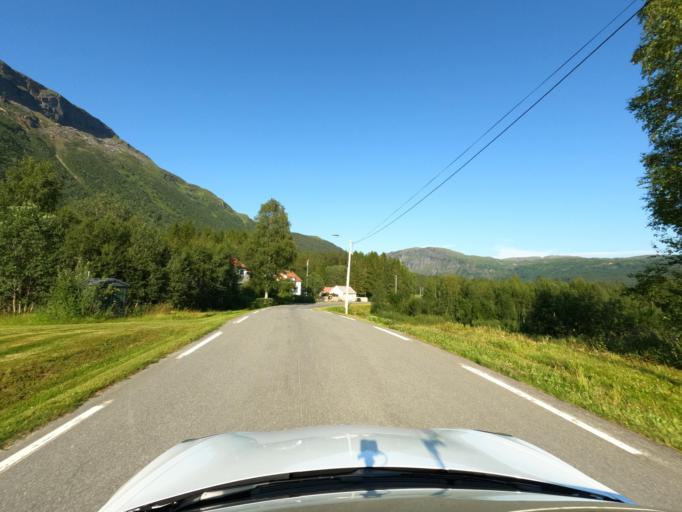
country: NO
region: Troms
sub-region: Gratangen
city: Gratangen
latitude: 68.5611
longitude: 17.6995
